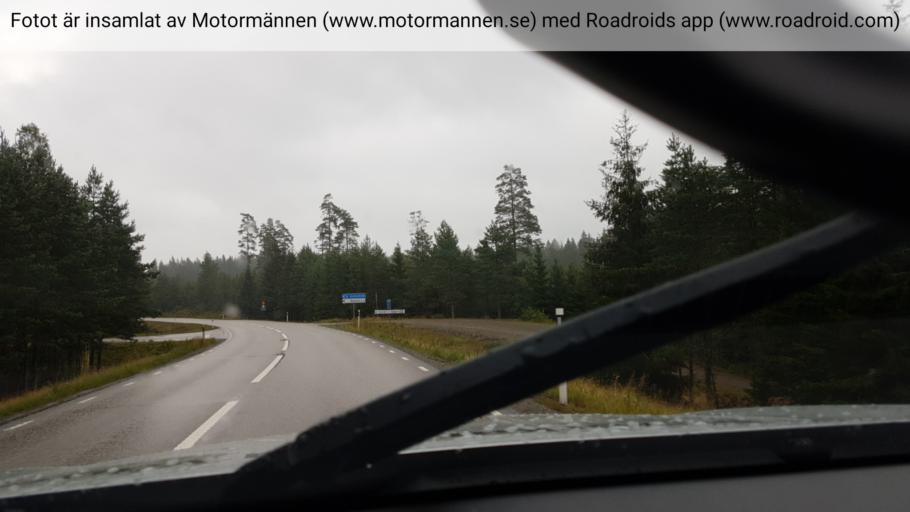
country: SE
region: Vaestra Goetaland
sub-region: Bengtsfors Kommun
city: Dals Langed
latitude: 58.8422
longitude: 12.1657
